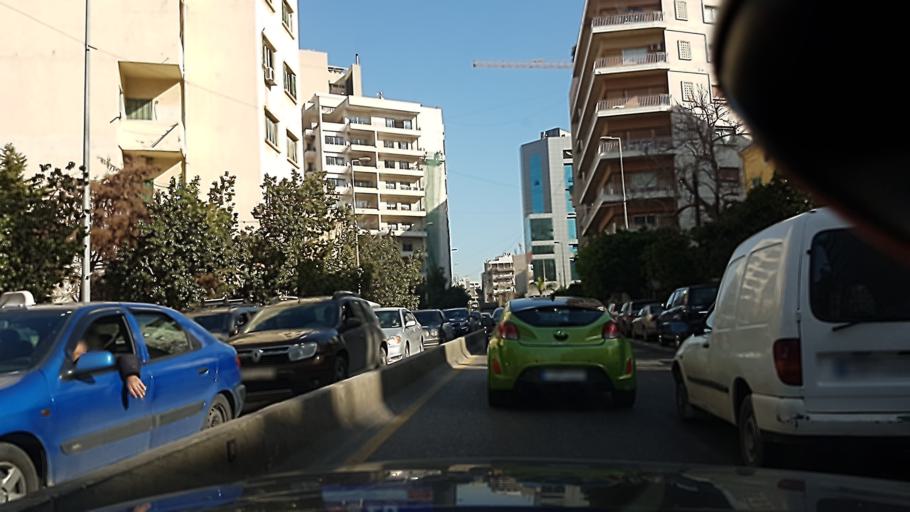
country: LB
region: Beyrouth
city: Beirut
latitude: 33.8922
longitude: 35.5132
